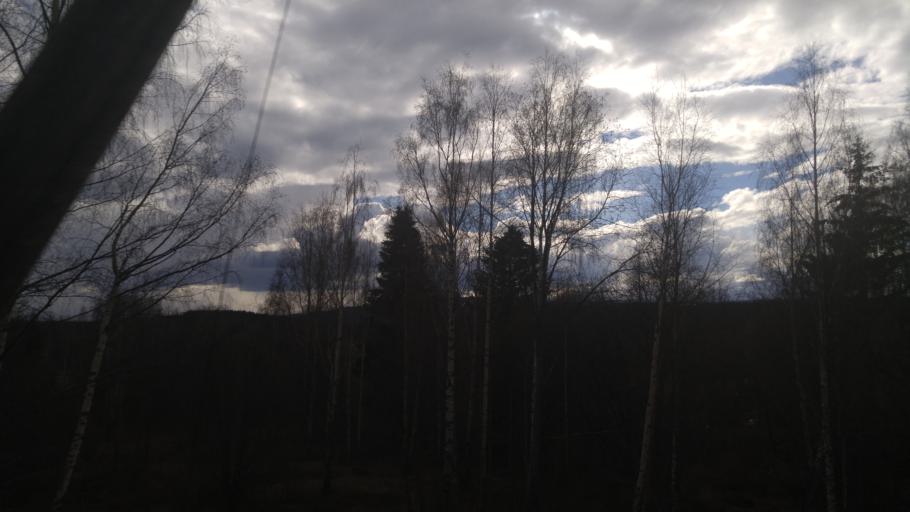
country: NO
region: Hedmark
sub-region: Stange
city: Stange
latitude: 60.6128
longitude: 11.2732
